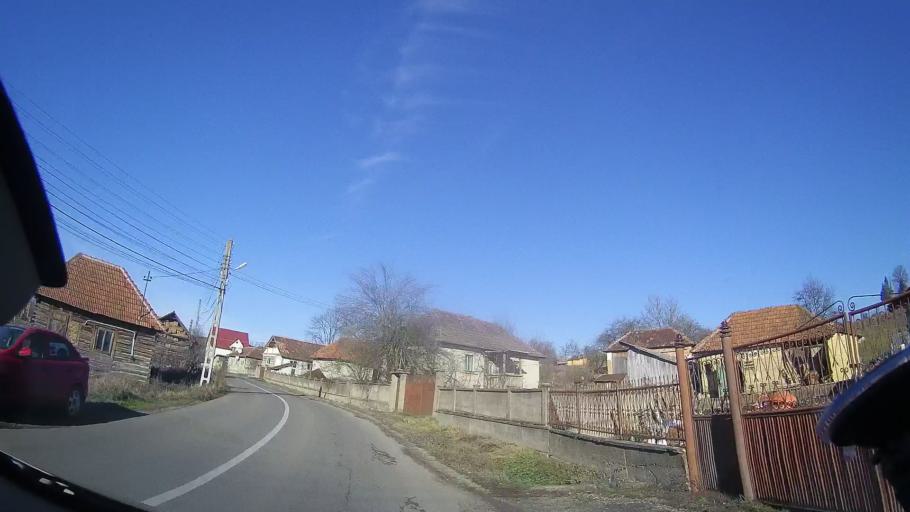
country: RO
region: Bihor
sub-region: Comuna Bratca
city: Beznea
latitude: 46.9531
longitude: 22.6118
